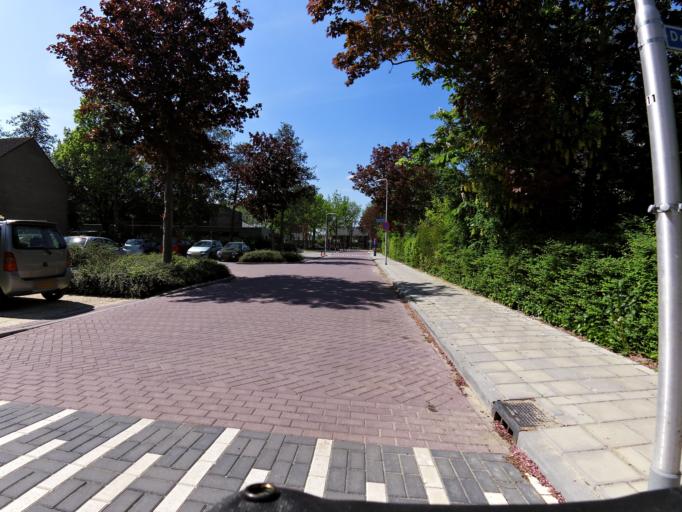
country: NL
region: South Holland
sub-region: Gemeente Binnenmaas
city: Heinenoord
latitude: 51.8261
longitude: 4.4801
